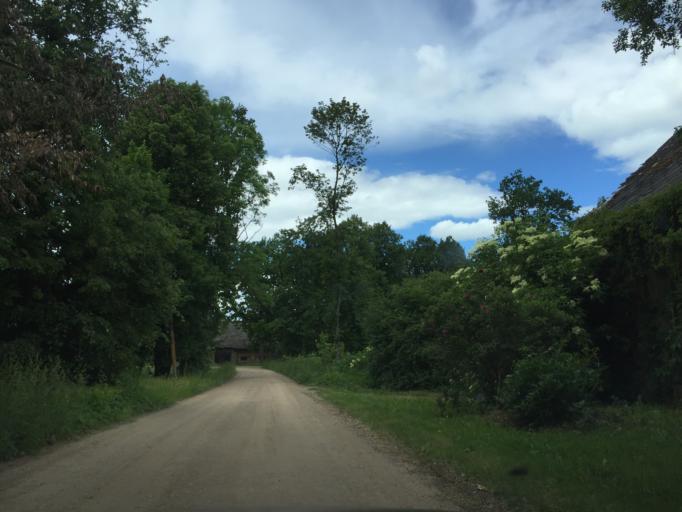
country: LV
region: Lecava
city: Iecava
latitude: 56.5837
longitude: 24.1982
